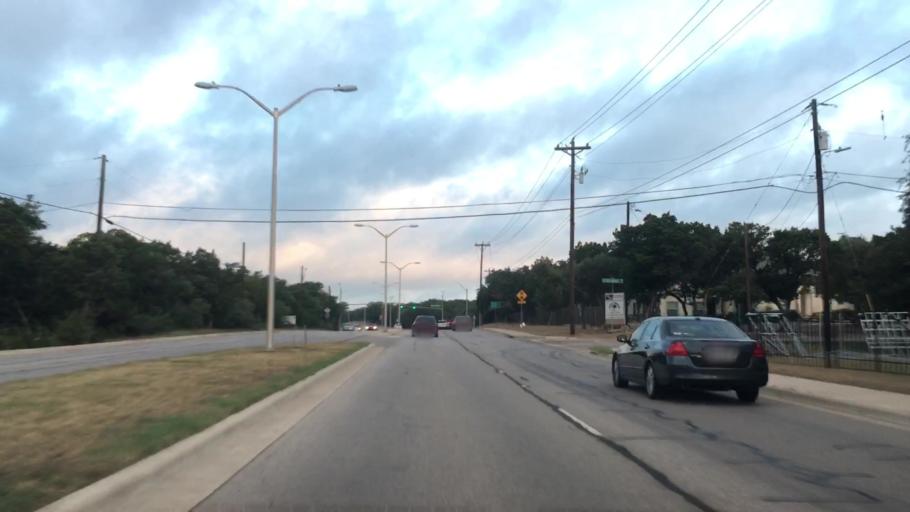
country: US
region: Texas
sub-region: Williamson County
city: Cedar Park
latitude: 30.5083
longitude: -97.7850
